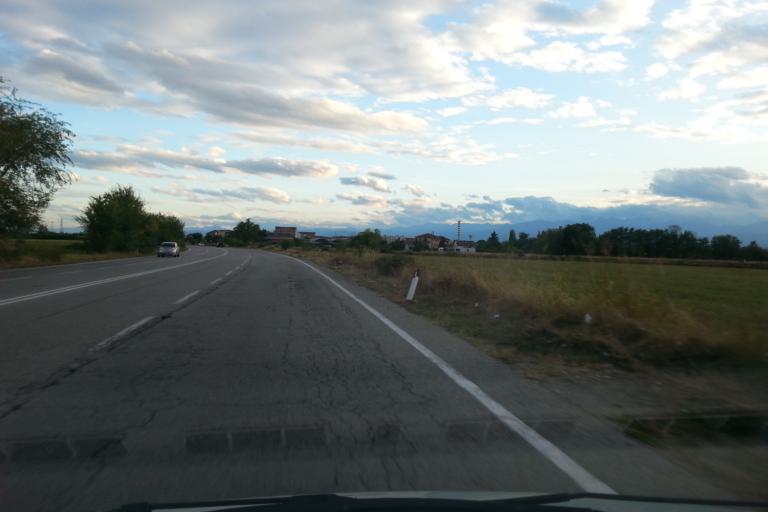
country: IT
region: Piedmont
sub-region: Provincia di Torino
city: Gerbole
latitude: 45.0075
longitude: 7.5193
